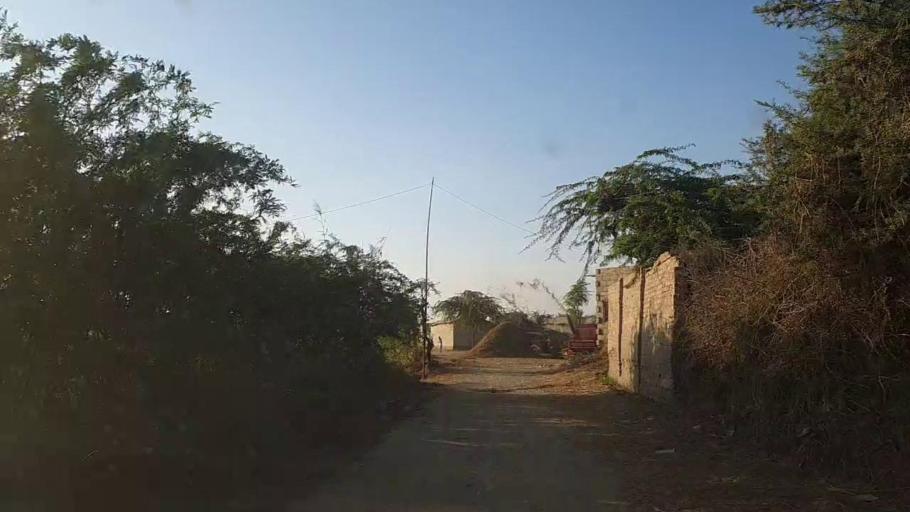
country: PK
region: Sindh
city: Mirpur Batoro
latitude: 24.6807
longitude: 68.2164
